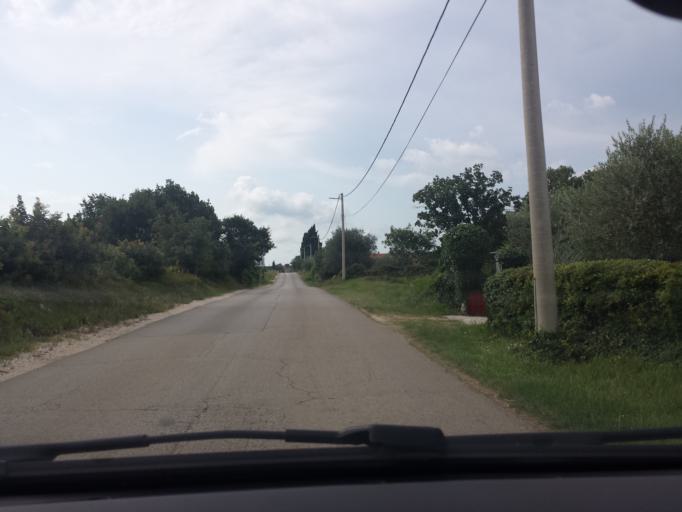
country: HR
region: Istarska
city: Galizana
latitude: 44.9395
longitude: 13.8678
